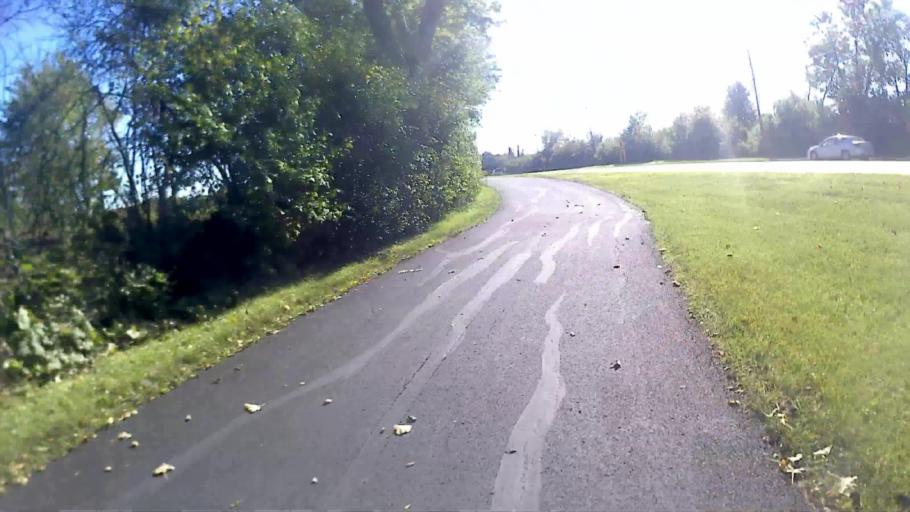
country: US
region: Illinois
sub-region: DuPage County
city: Addison
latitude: 41.9446
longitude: -87.9885
